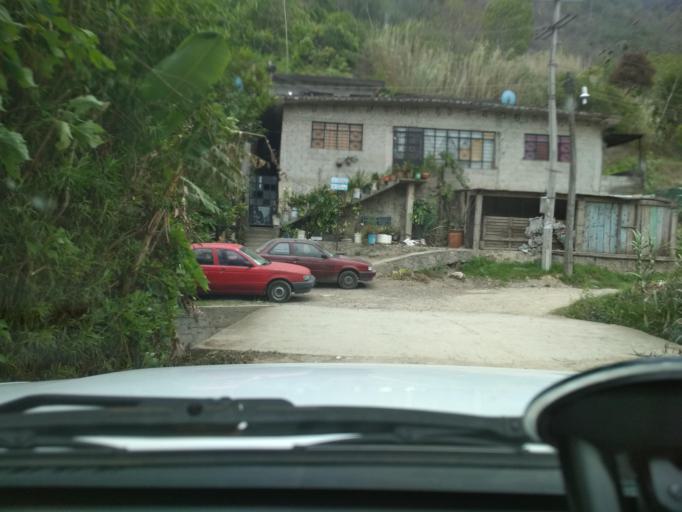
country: MX
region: Veracruz
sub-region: Nogales
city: Taza de Agua Ojo Zarco
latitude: 18.7746
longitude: -97.2091
